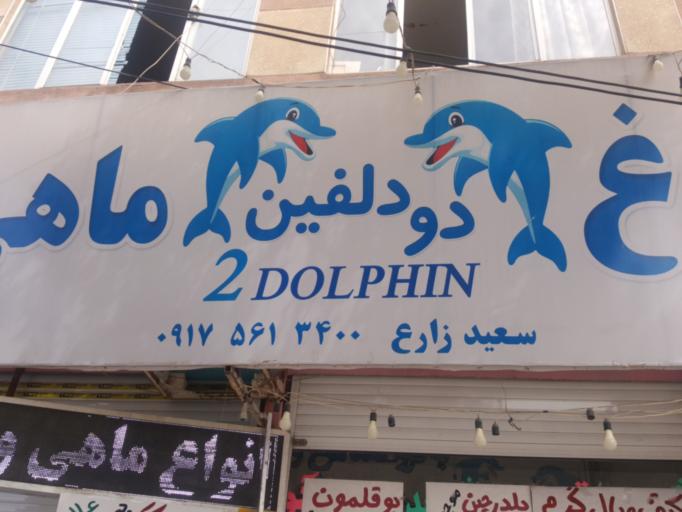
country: IR
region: Fars
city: Marvdasht
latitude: 29.8797
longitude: 52.8078
